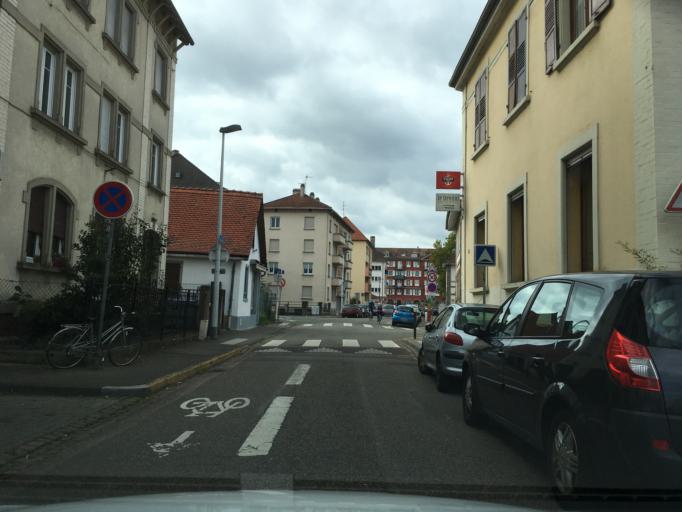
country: FR
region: Alsace
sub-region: Departement du Bas-Rhin
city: Strasbourg
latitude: 48.5635
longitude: 7.7647
